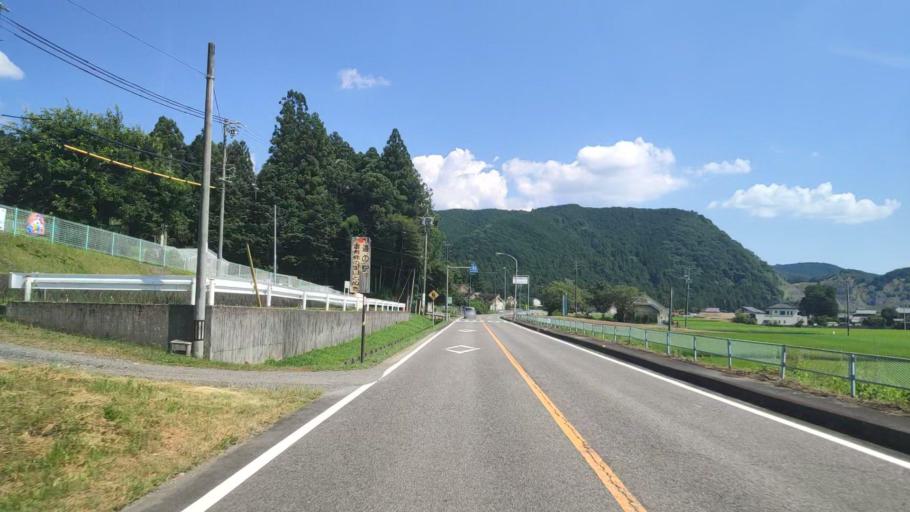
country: JP
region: Gifu
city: Godo
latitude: 35.5374
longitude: 136.6490
